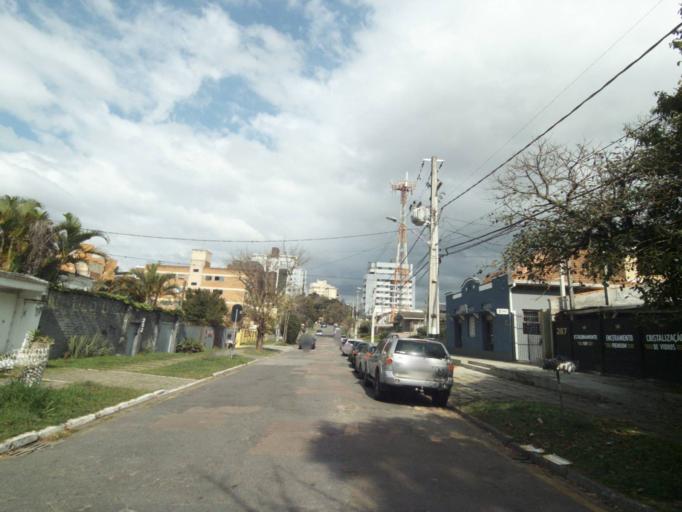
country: BR
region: Parana
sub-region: Curitiba
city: Curitiba
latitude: -25.4045
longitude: -49.2586
